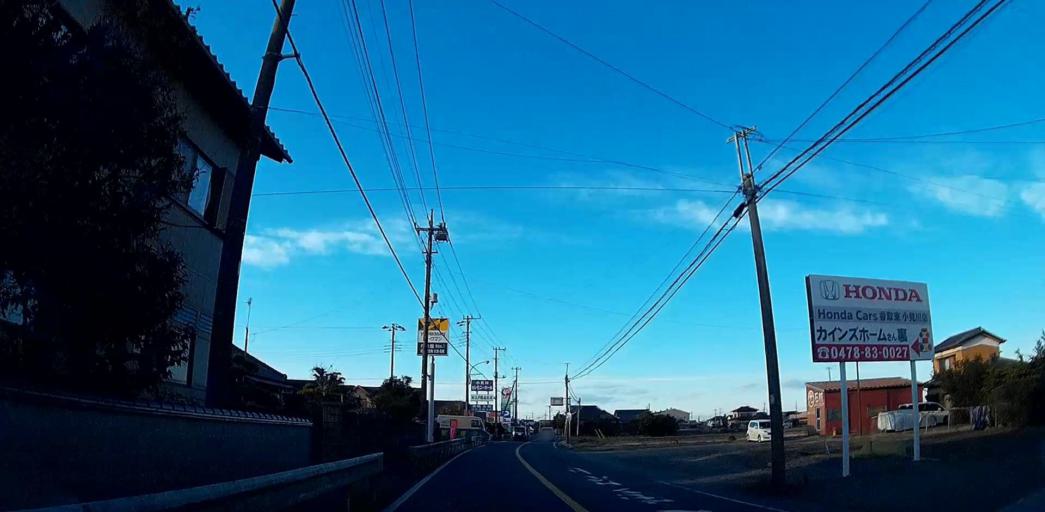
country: JP
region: Chiba
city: Omigawa
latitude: 35.8621
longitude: 140.5980
